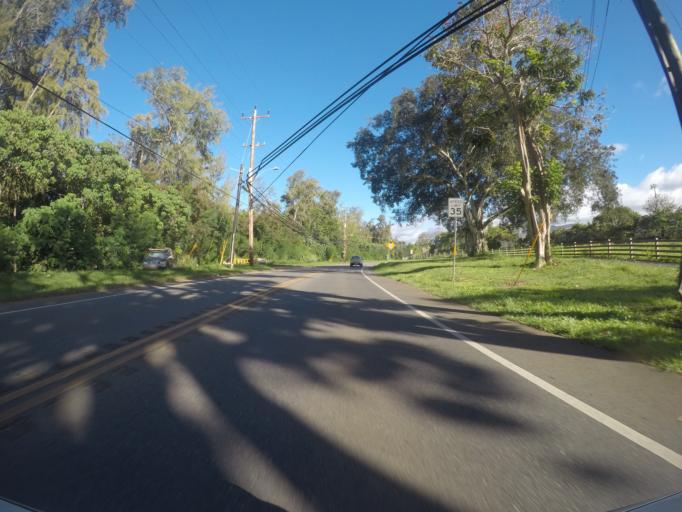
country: US
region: Hawaii
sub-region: Honolulu County
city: La'ie
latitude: 21.6571
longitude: -157.9311
